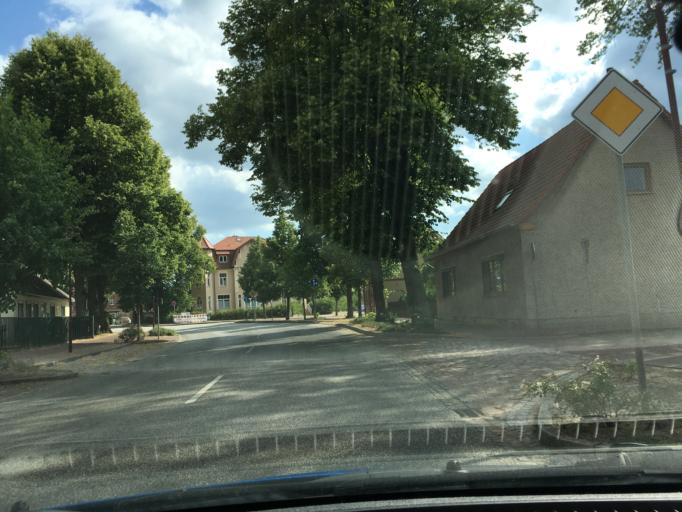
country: DE
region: Mecklenburg-Vorpommern
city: Lubtheen
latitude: 53.3014
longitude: 11.0827
